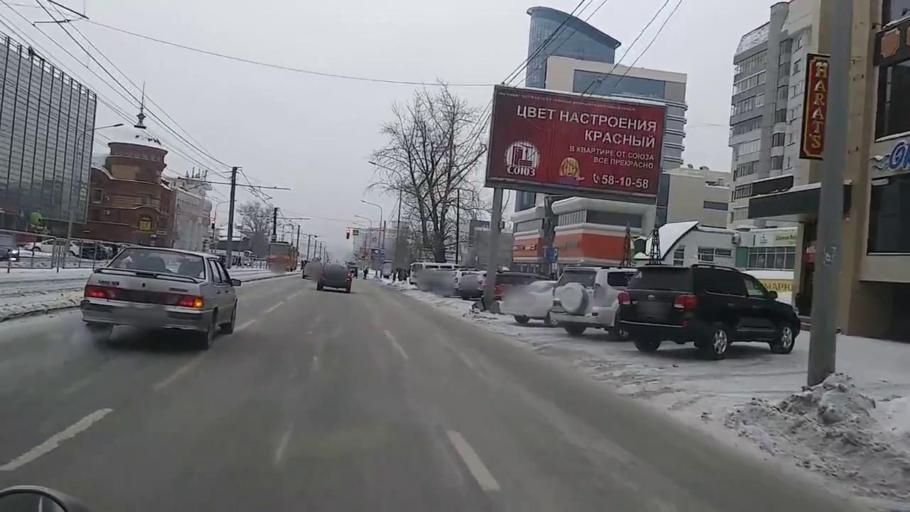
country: RU
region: Altai Krai
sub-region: Gorod Barnaulskiy
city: Barnaul
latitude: 53.3385
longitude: 83.7735
